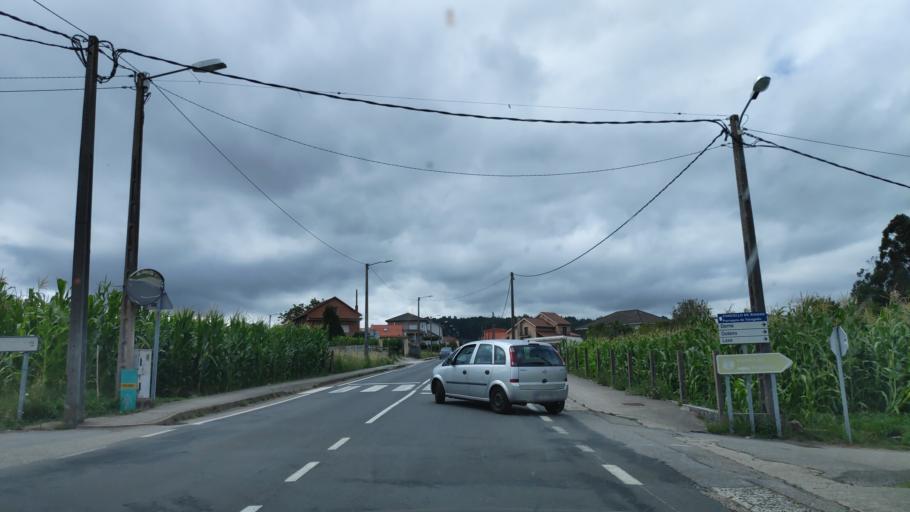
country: ES
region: Galicia
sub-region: Provincia da Coruna
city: Rianxo
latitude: 42.6703
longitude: -8.8157
